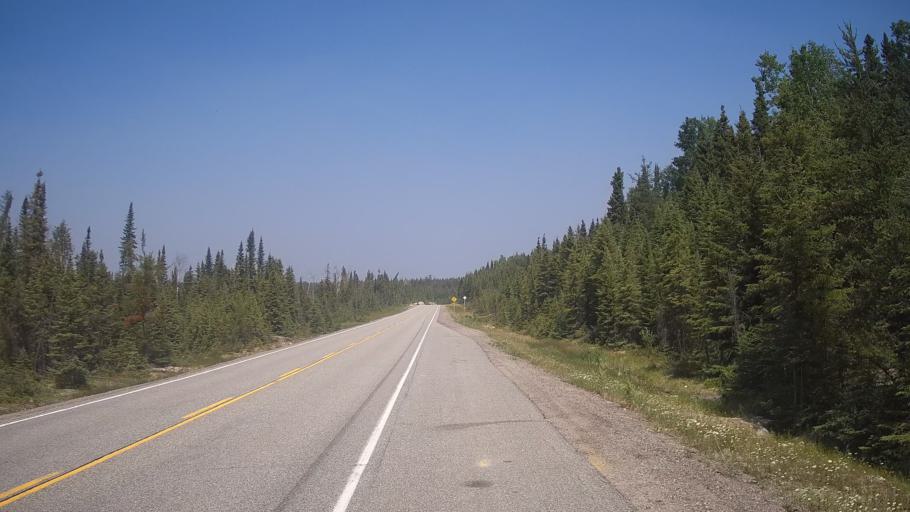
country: CA
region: Ontario
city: Timmins
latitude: 48.0714
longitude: -81.5918
